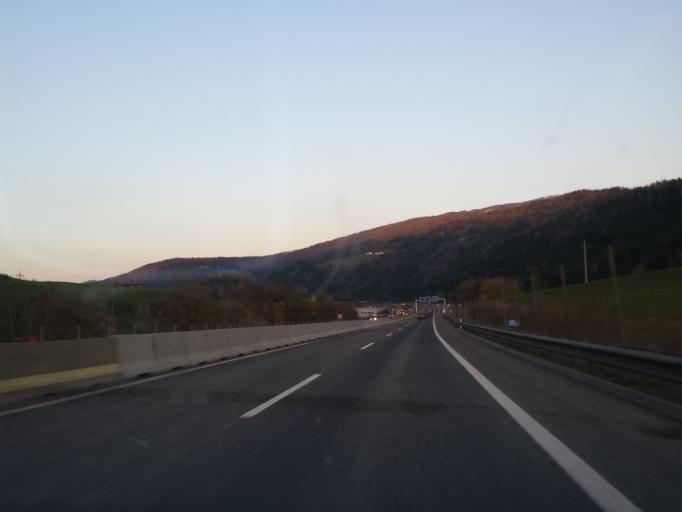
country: AT
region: Styria
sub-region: Politischer Bezirk Bruck-Muerzzuschlag
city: Muerzzuschlag
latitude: 47.6031
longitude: 15.7123
